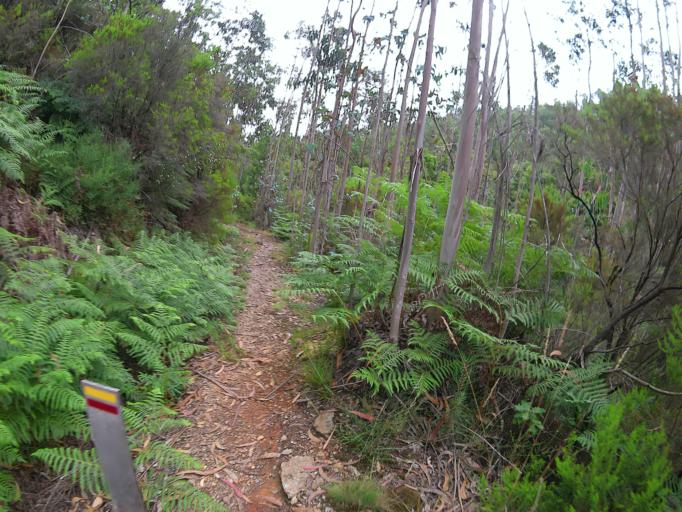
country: PT
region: Aveiro
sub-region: Albergaria-A-Velha
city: Branca
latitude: 40.7494
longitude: -8.4298
